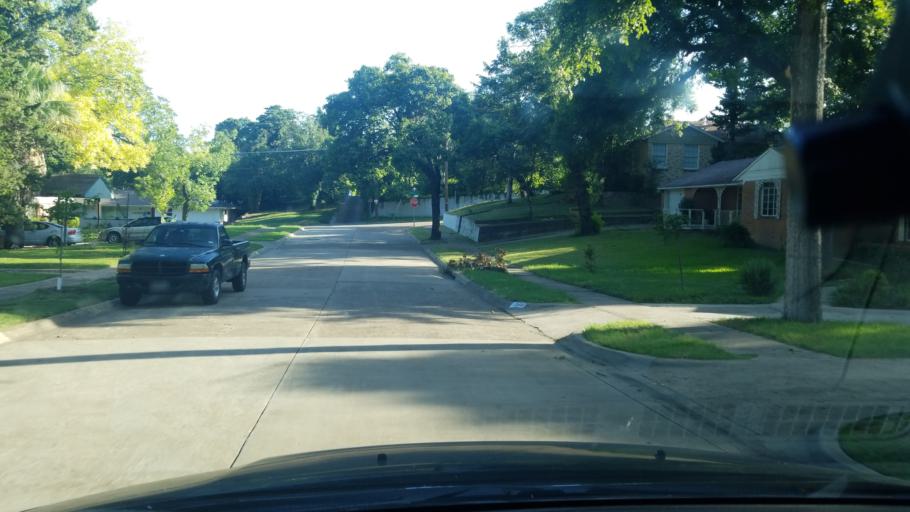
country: US
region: Texas
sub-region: Dallas County
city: Dallas
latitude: 32.7325
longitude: -96.8168
